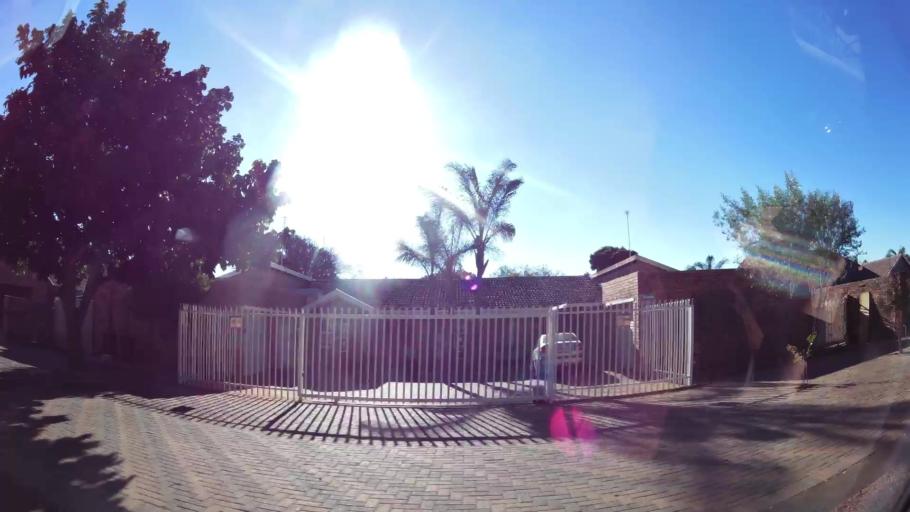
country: ZA
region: Limpopo
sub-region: Capricorn District Municipality
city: Polokwane
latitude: -23.8977
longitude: 29.4783
